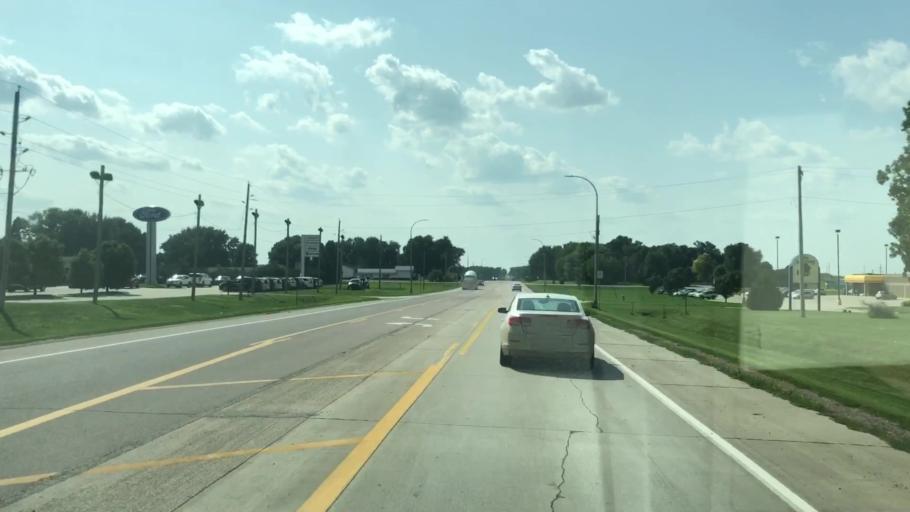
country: US
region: Iowa
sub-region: O'Brien County
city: Sheldon
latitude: 43.1861
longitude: -95.8185
